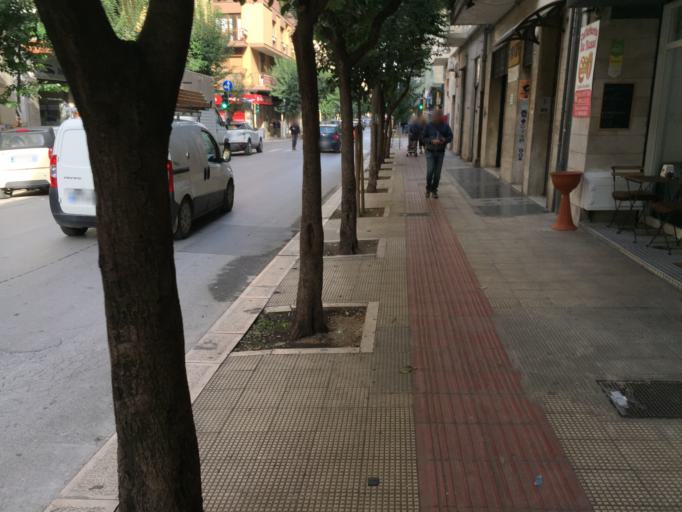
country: IT
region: Apulia
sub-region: Provincia di Bari
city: Bari
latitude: 41.1233
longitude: 16.8654
